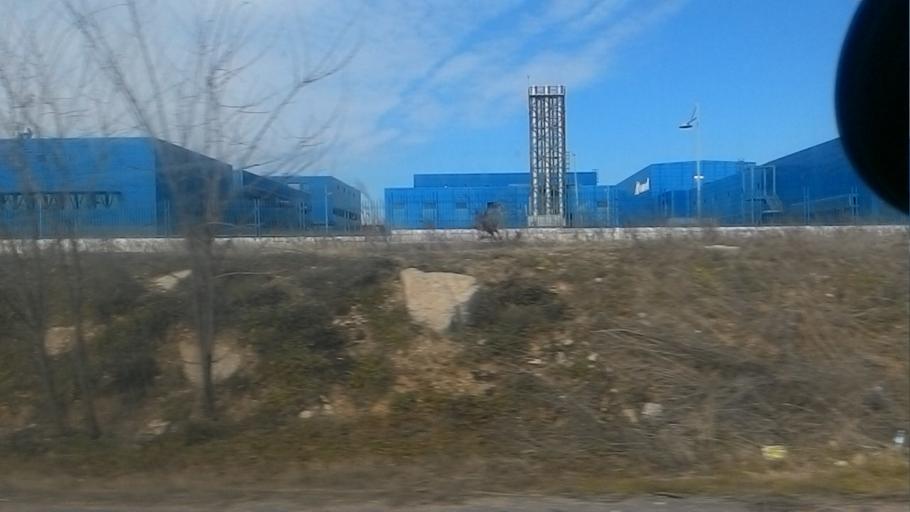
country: TR
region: Istanbul
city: Canta
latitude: 41.0818
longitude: 28.0499
